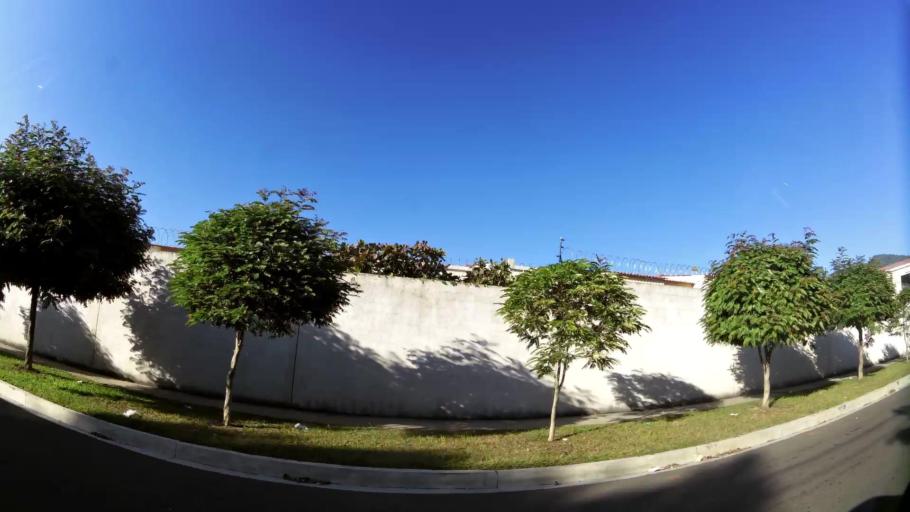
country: SV
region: La Libertad
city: Santa Tecla
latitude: 13.7386
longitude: -89.3506
